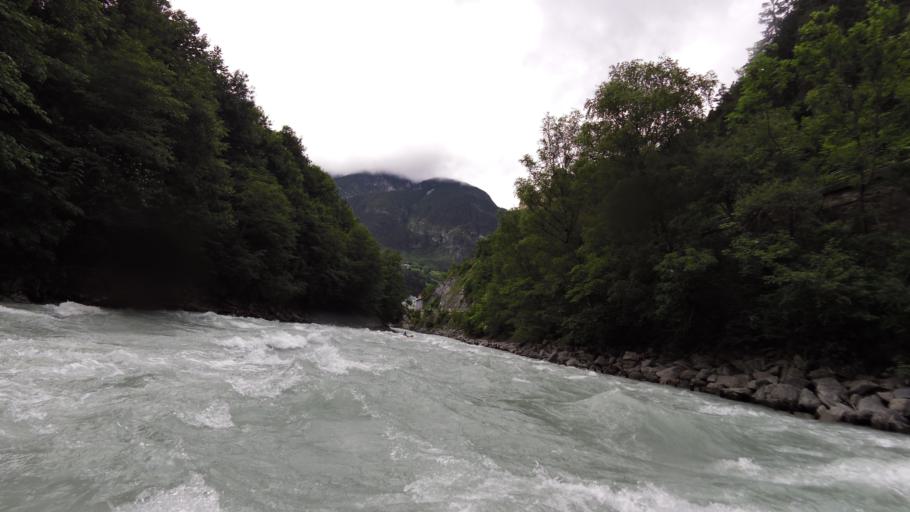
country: AT
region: Tyrol
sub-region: Politischer Bezirk Landeck
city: Landeck
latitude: 47.1332
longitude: 10.5688
